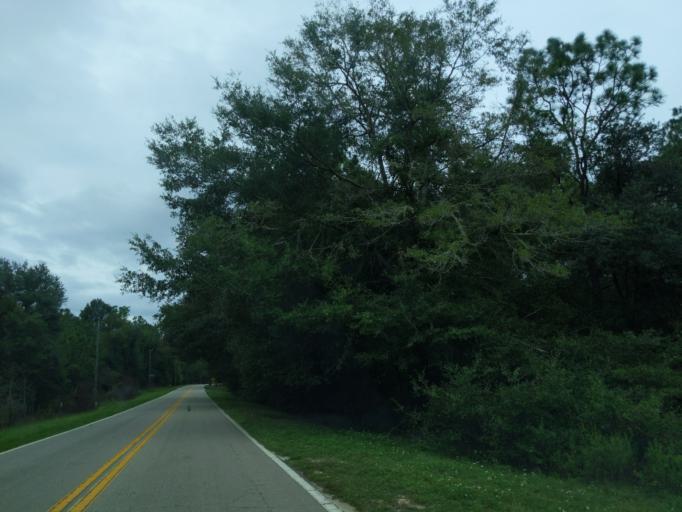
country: US
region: Florida
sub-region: Gadsden County
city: Midway
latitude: 30.4265
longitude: -84.4133
